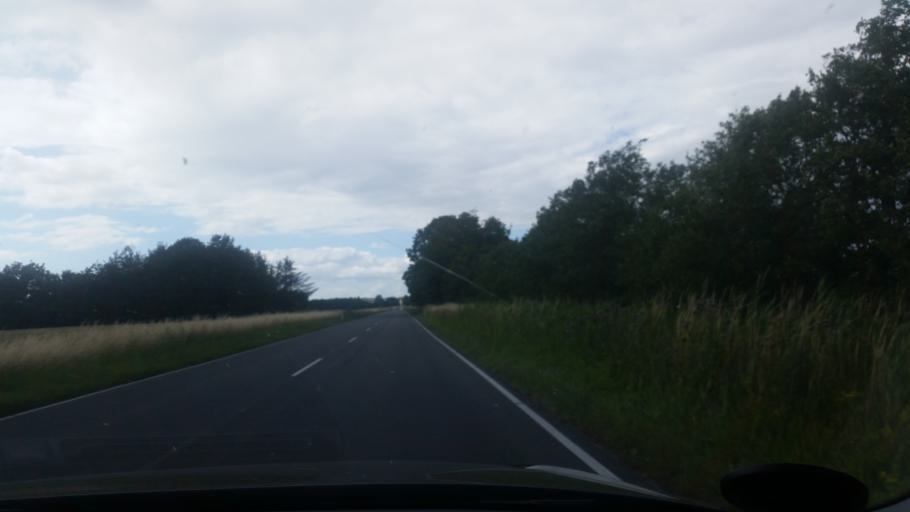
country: DK
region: Zealand
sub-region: Odsherred Kommune
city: Asnaes
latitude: 55.7694
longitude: 11.4940
